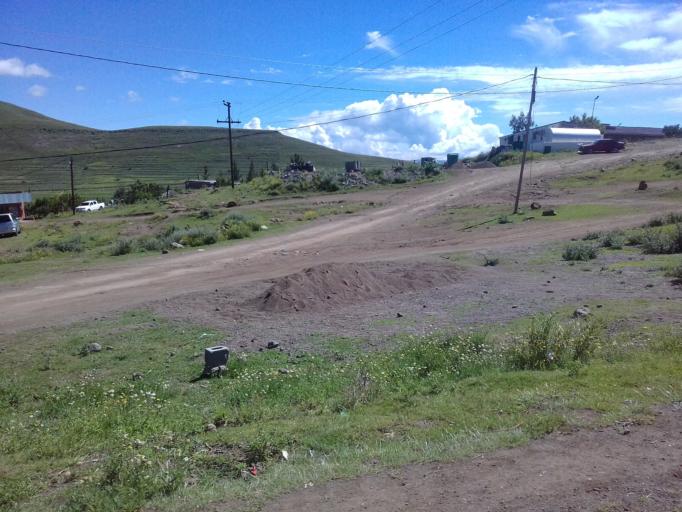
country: LS
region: Thaba-Tseka
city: Thaba-Tseka
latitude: -29.5154
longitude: 28.5938
